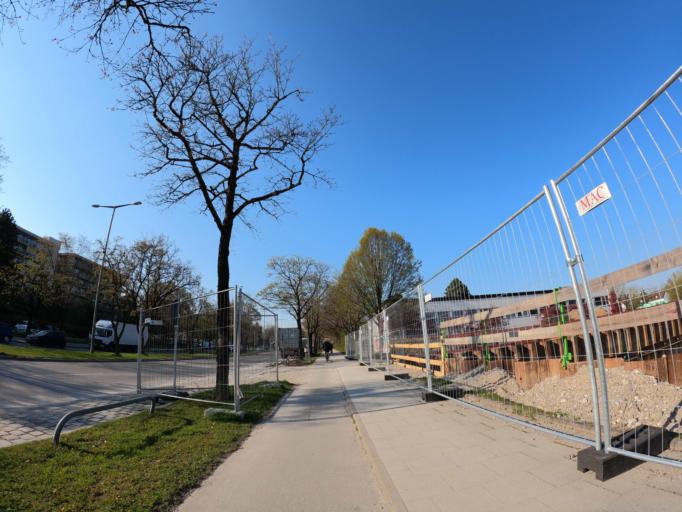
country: DE
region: Bavaria
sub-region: Upper Bavaria
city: Neubiberg
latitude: 48.1044
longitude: 11.6592
